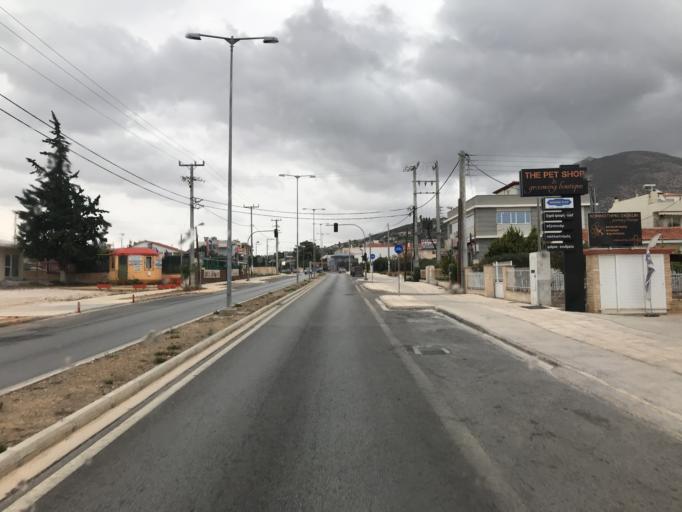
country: GR
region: Attica
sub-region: Nomarchia Anatolikis Attikis
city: Agios Dimitrios Kropias
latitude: 37.7925
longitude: 23.8897
